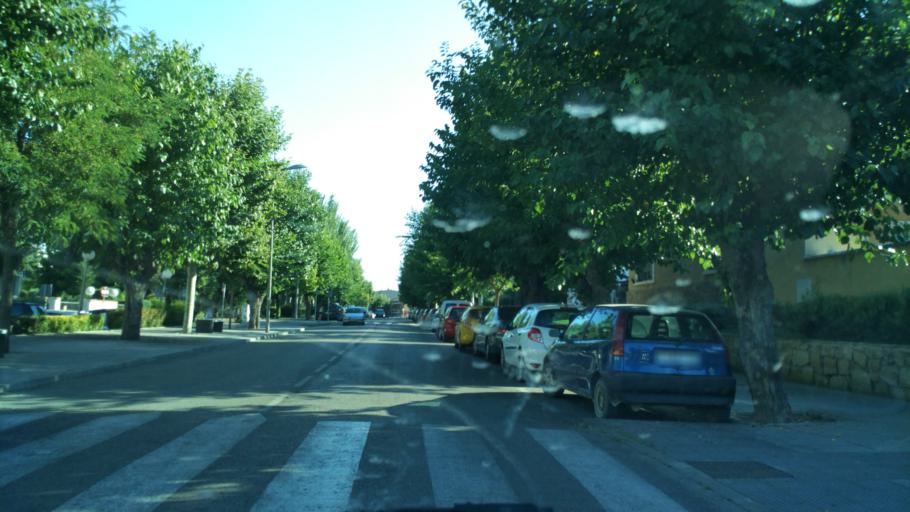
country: ES
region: Madrid
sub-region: Provincia de Madrid
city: San Agustin de Guadalix
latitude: 40.6823
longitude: -3.6128
